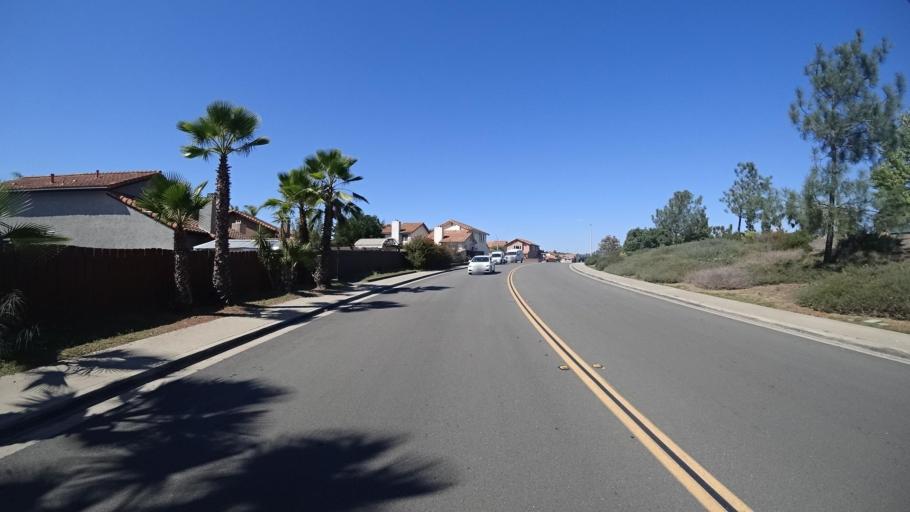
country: US
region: California
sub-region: San Diego County
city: Rancho San Diego
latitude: 32.7440
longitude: -116.9241
